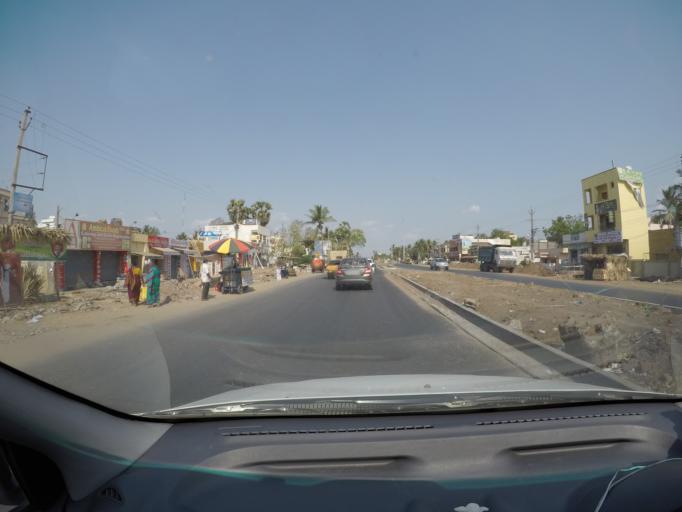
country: IN
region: Andhra Pradesh
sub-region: Krishna
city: Yanamalakuduru
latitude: 16.4762
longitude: 80.7071
